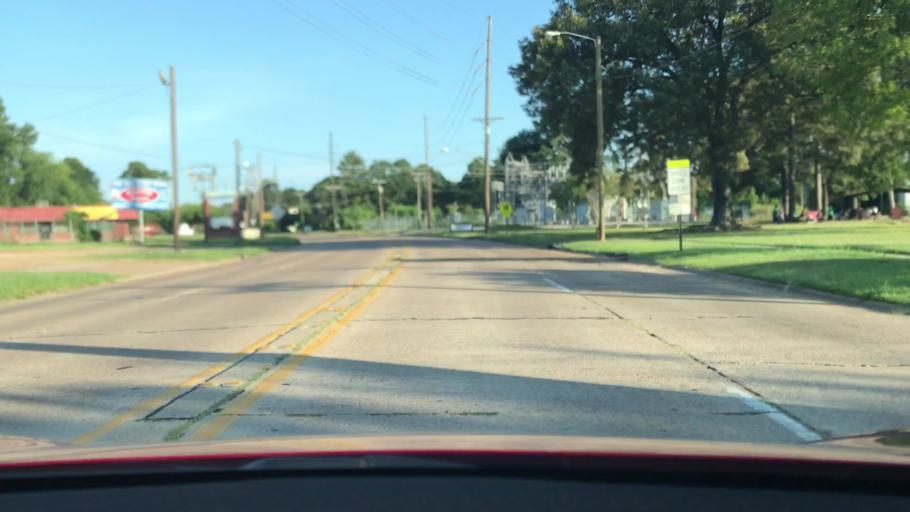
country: US
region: Louisiana
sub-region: Bossier Parish
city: Bossier City
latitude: 32.4319
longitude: -93.7458
